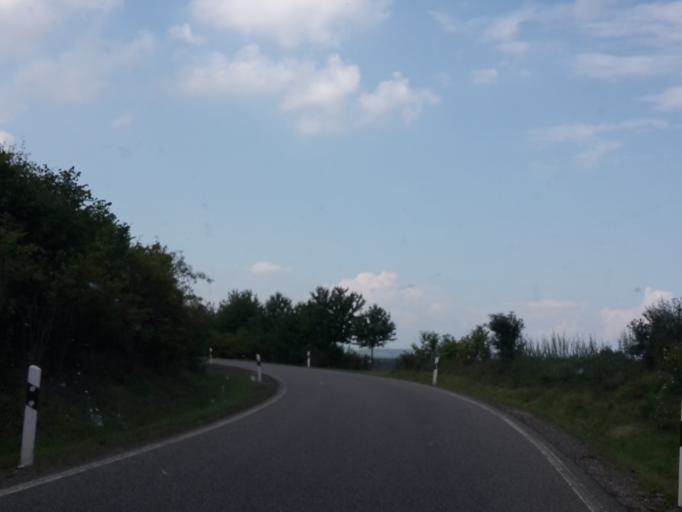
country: DE
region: Rheinland-Pfalz
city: Lonsheim
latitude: 49.7900
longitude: 8.0929
